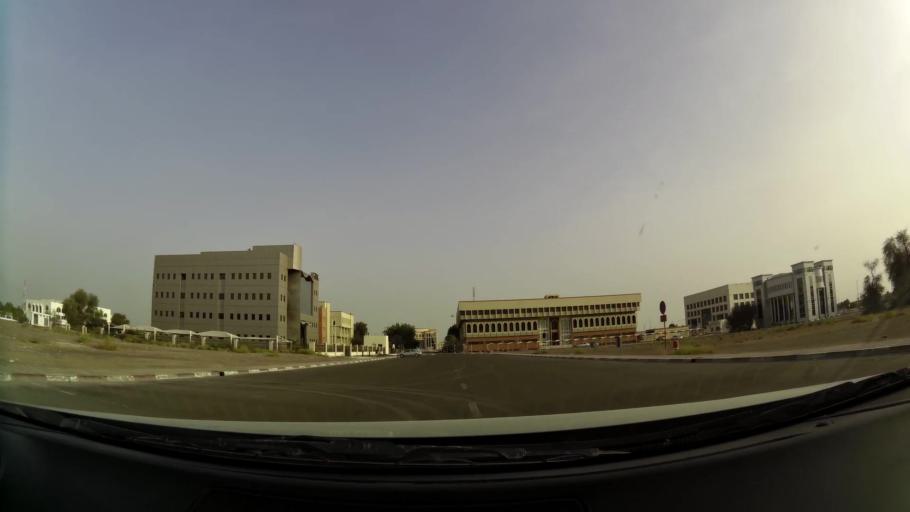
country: AE
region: Abu Dhabi
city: Al Ain
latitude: 24.2395
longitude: 55.7326
